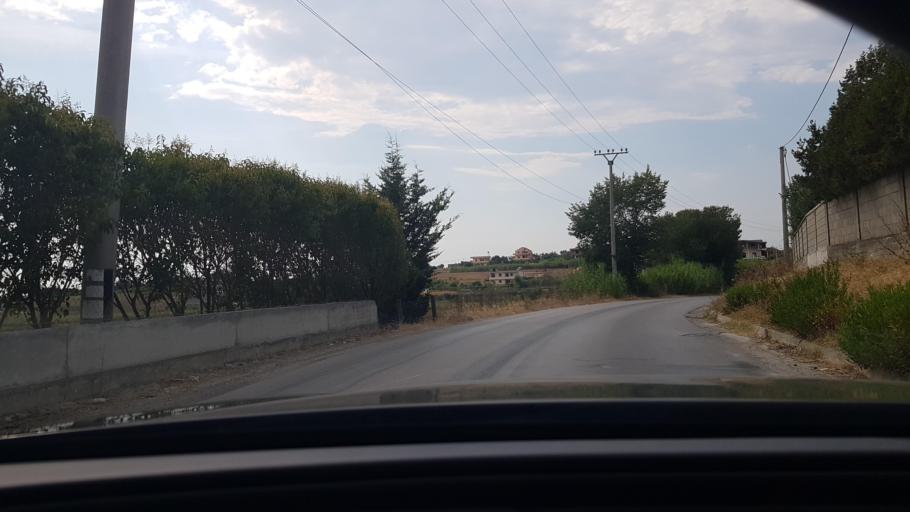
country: AL
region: Durres
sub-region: Rrethi i Durresit
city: Katundi i Ri
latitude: 41.4273
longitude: 19.5457
